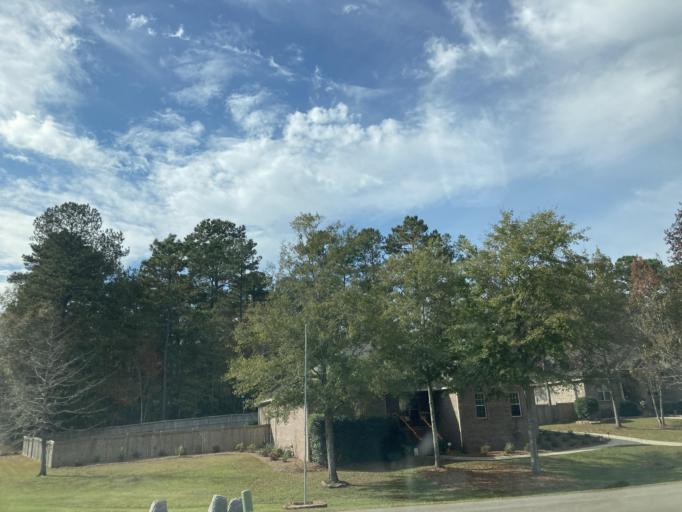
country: US
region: Mississippi
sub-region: Lamar County
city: West Hattiesburg
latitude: 31.3332
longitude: -89.4367
